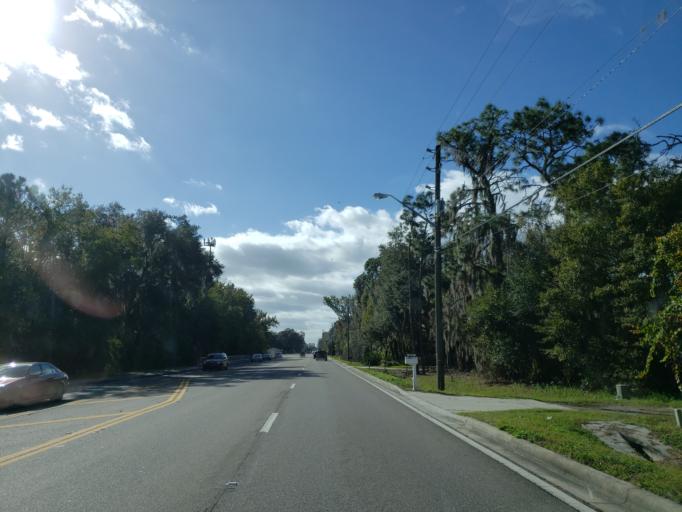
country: US
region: Florida
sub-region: Polk County
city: Medulla
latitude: 27.9843
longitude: -81.9733
